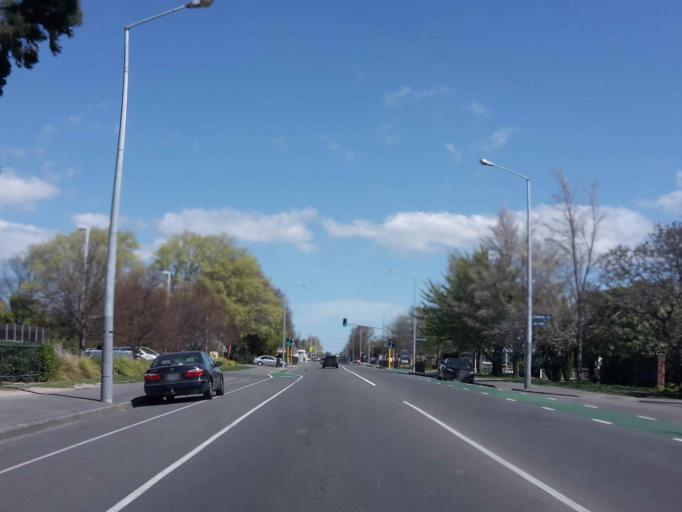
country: NZ
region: Canterbury
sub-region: Selwyn District
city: Prebbleton
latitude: -43.5343
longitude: 172.5634
